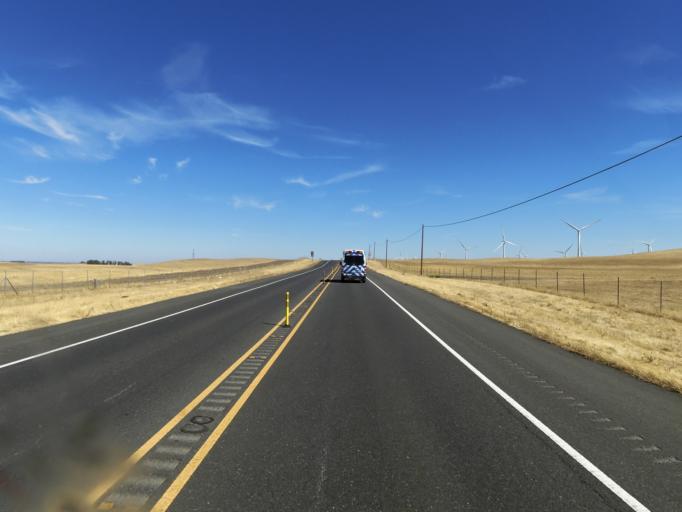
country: US
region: California
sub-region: Solano County
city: Rio Vista
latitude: 38.1837
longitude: -121.8370
